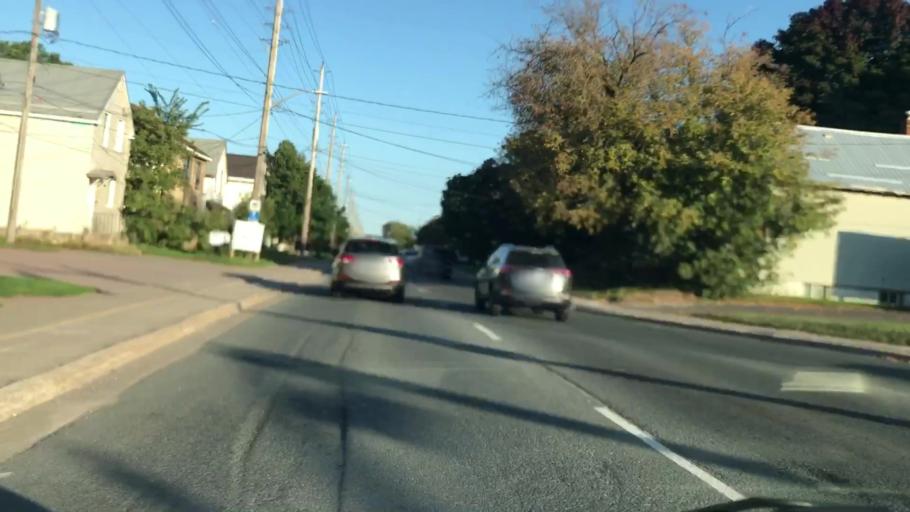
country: CA
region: Ontario
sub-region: Algoma
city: Sault Ste. Marie
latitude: 46.5154
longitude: -84.3332
